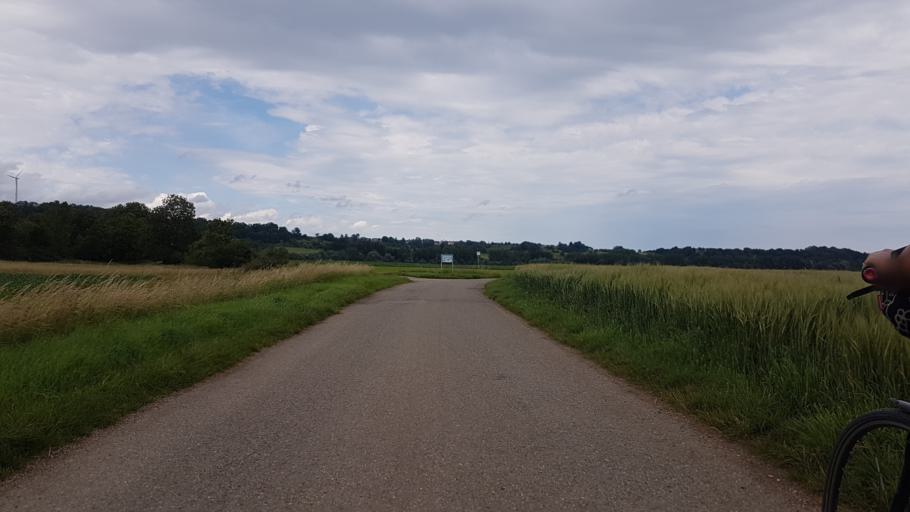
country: DE
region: Baden-Wuerttemberg
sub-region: Tuebingen Region
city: Mengen
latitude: 48.0618
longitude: 9.3601
